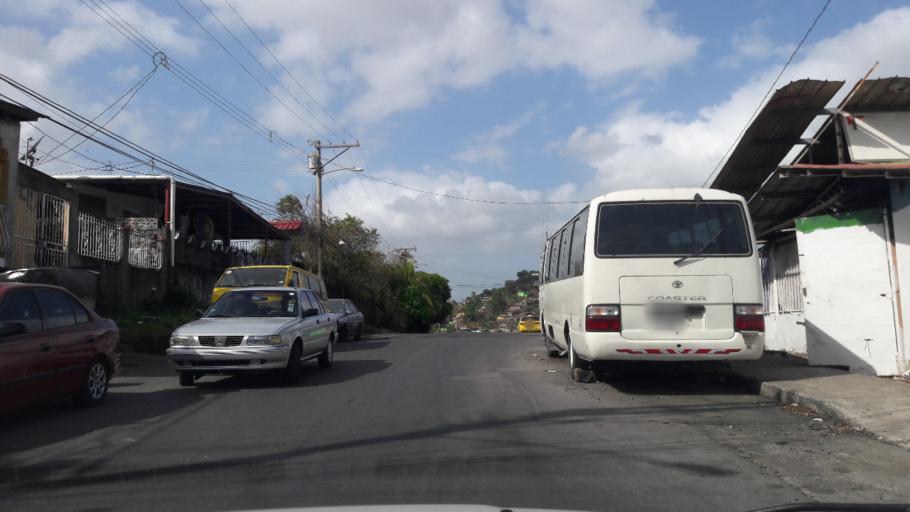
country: PA
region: Panama
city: San Miguelito
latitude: 9.0468
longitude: -79.5105
